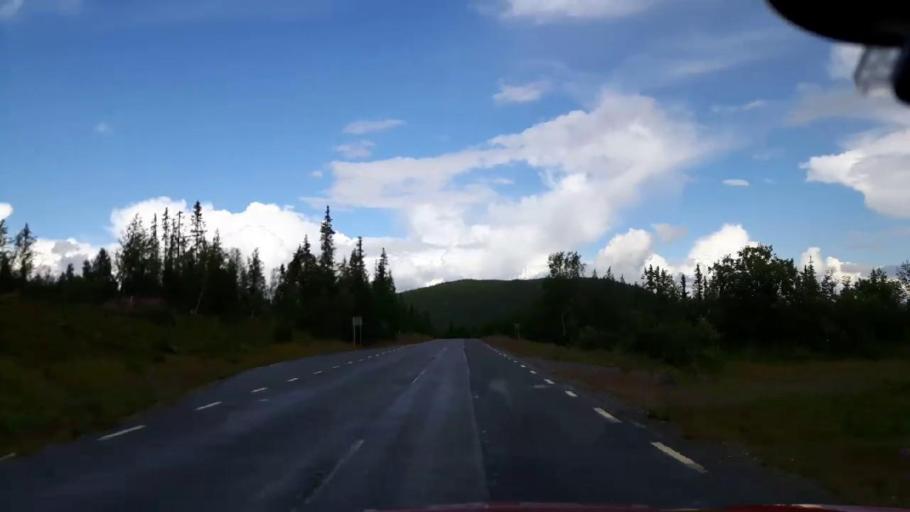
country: SE
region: Vaesterbotten
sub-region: Vilhelmina Kommun
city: Sjoberg
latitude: 65.0153
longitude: 15.1705
